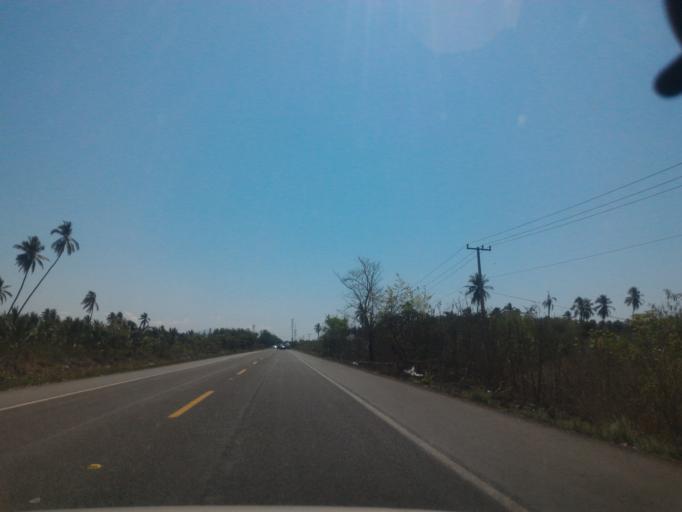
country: MX
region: Colima
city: Tecoman
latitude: 18.8395
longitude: -103.8218
